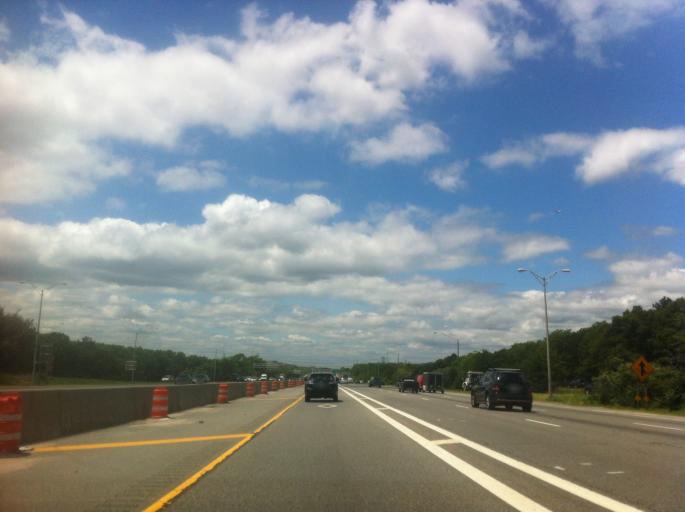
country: US
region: New York
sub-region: Suffolk County
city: Holtsville
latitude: 40.8191
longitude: -73.0605
